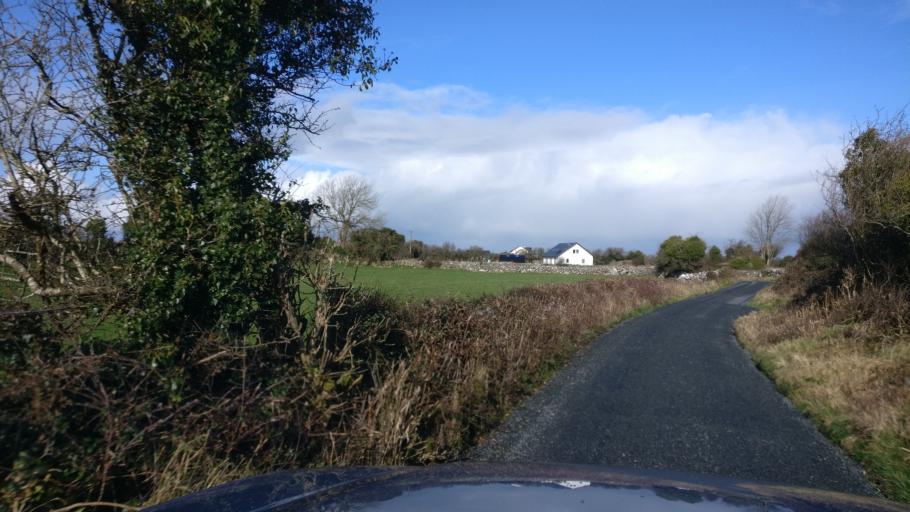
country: IE
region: Connaught
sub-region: County Galway
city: Athenry
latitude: 53.2366
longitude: -8.7738
